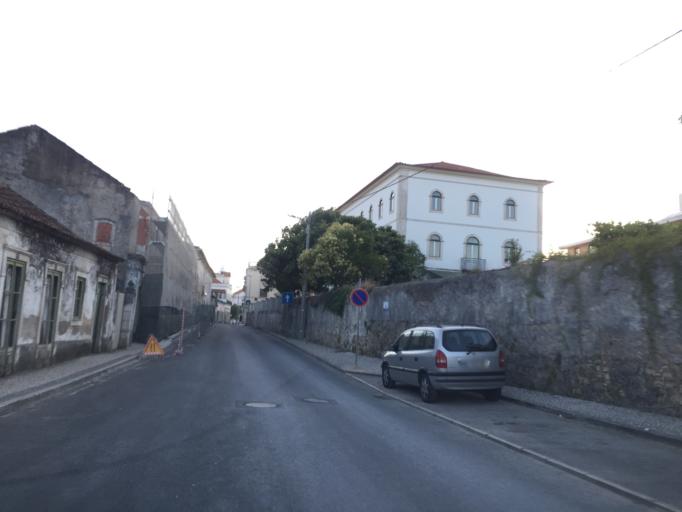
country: PT
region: Santarem
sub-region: Ourem
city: Ourem
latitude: 39.6563
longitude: -8.5748
